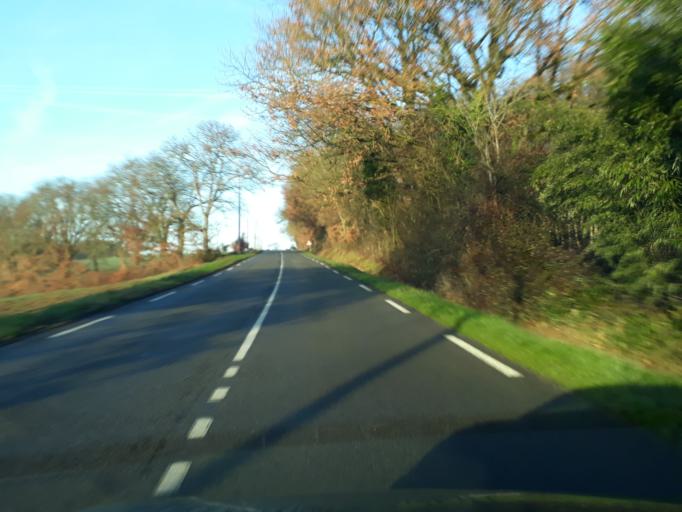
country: FR
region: Midi-Pyrenees
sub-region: Departement de la Haute-Garonne
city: Berat
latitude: 43.3866
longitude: 1.1654
